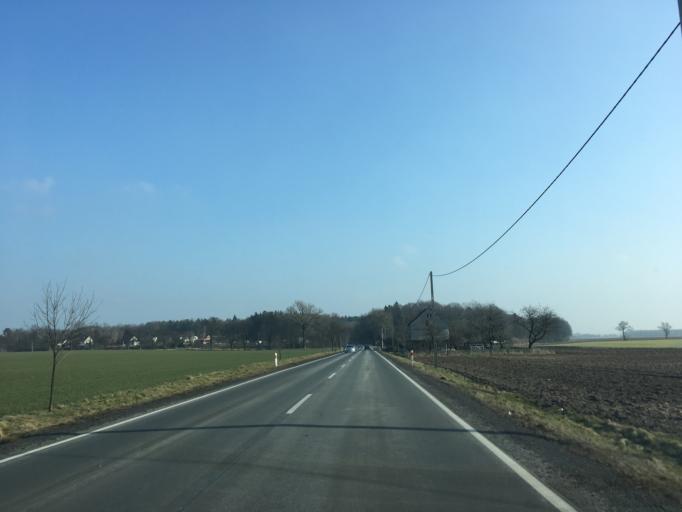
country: PL
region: Lower Silesian Voivodeship
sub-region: Powiat legnicki
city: Chojnow
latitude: 51.2761
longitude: 15.8691
